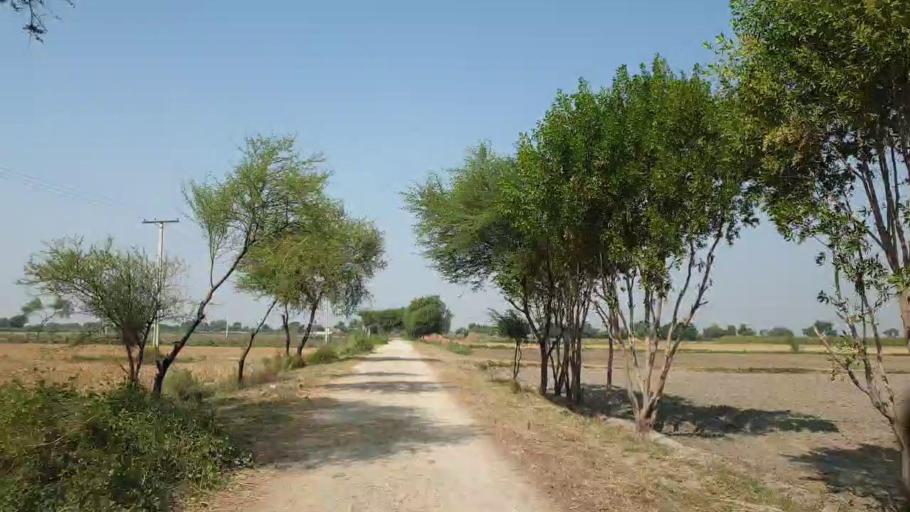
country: PK
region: Sindh
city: Tando Muhammad Khan
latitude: 25.0307
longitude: 68.4056
